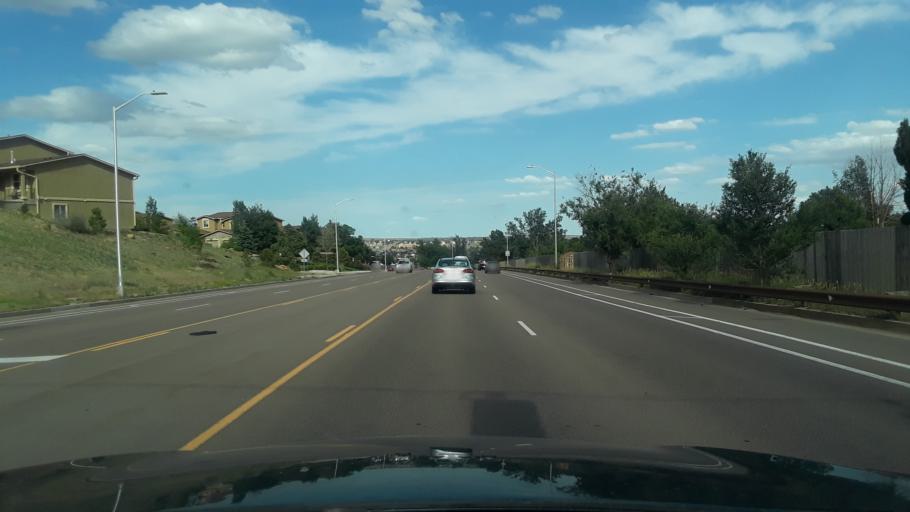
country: US
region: Colorado
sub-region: El Paso County
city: Cimarron Hills
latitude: 38.8851
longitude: -104.7271
